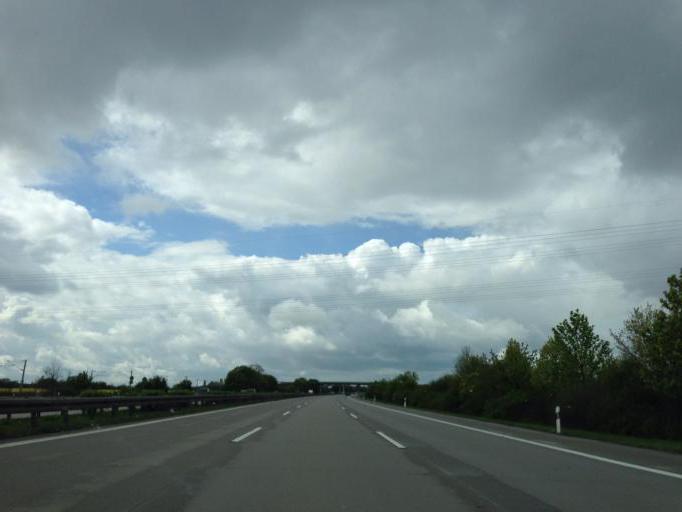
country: DE
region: Saxony
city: Zwochau
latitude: 51.4159
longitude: 12.2896
